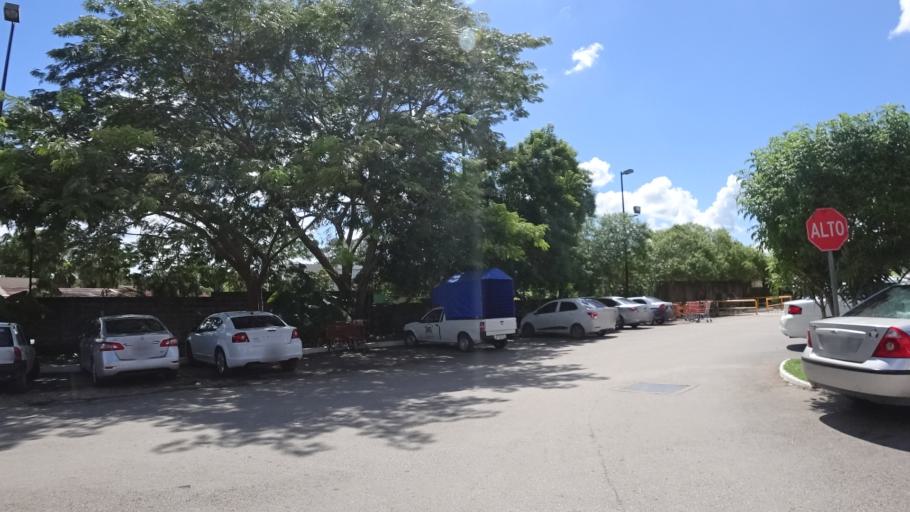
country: MX
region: Yucatan
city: Valladolid
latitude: 20.7019
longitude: -88.2019
